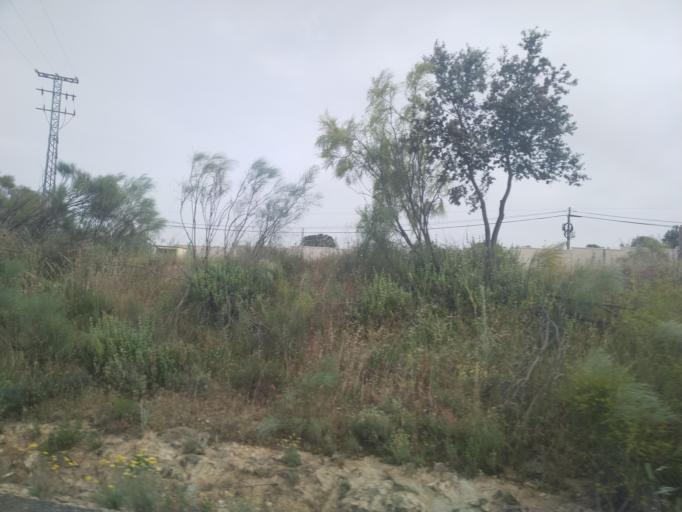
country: ES
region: Castille-La Mancha
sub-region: Province of Toledo
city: Guadamur
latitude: 39.8109
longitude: -4.1161
